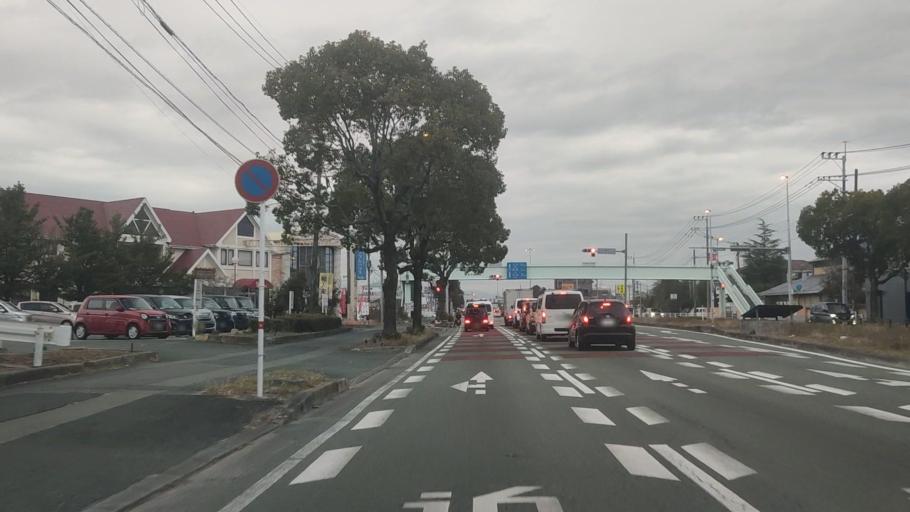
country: JP
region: Kumamoto
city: Kumamoto
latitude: 32.7704
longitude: 130.7293
